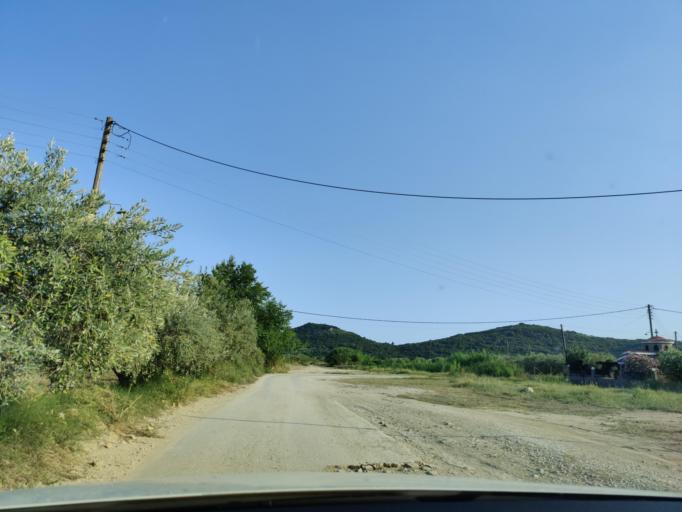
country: GR
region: East Macedonia and Thrace
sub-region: Nomos Kavalas
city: Nea Peramos
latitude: 40.8303
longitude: 24.3031
